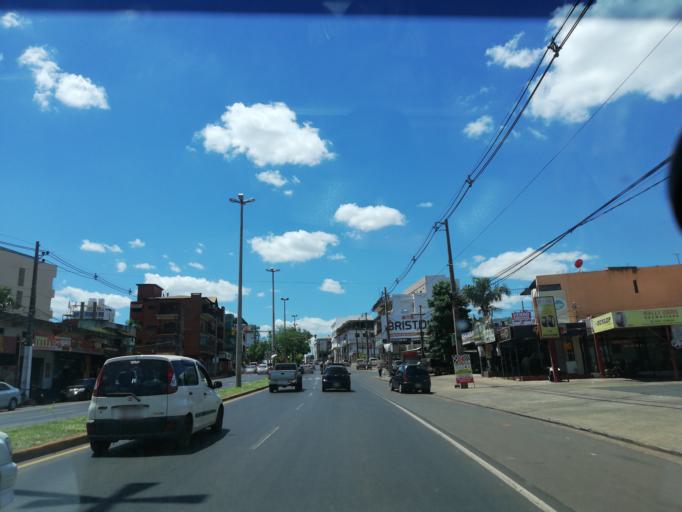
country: PY
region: Itapua
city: Encarnacion
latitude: -27.3440
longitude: -55.8577
